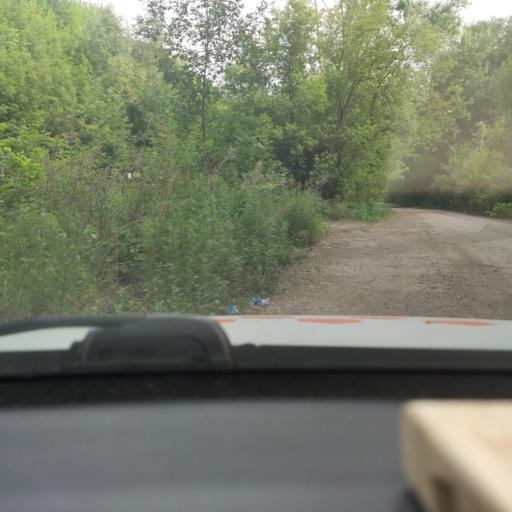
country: RU
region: Bashkortostan
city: Ufa
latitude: 54.7226
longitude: 55.9154
